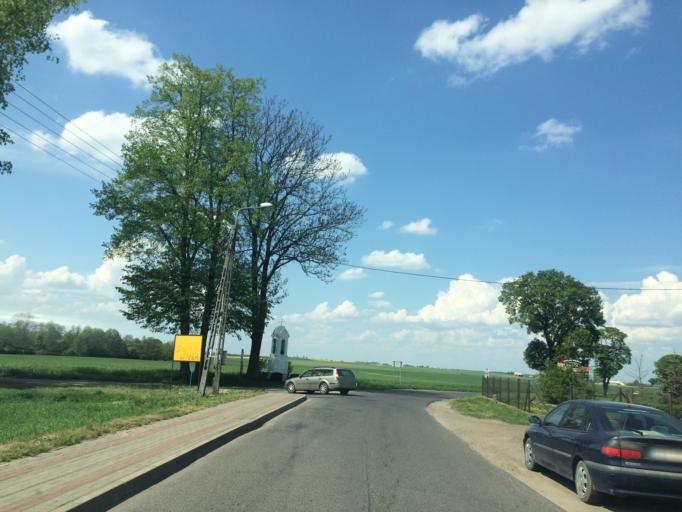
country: PL
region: Warmian-Masurian Voivodeship
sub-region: Powiat ilawski
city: Lubawa
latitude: 53.4137
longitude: 19.7539
